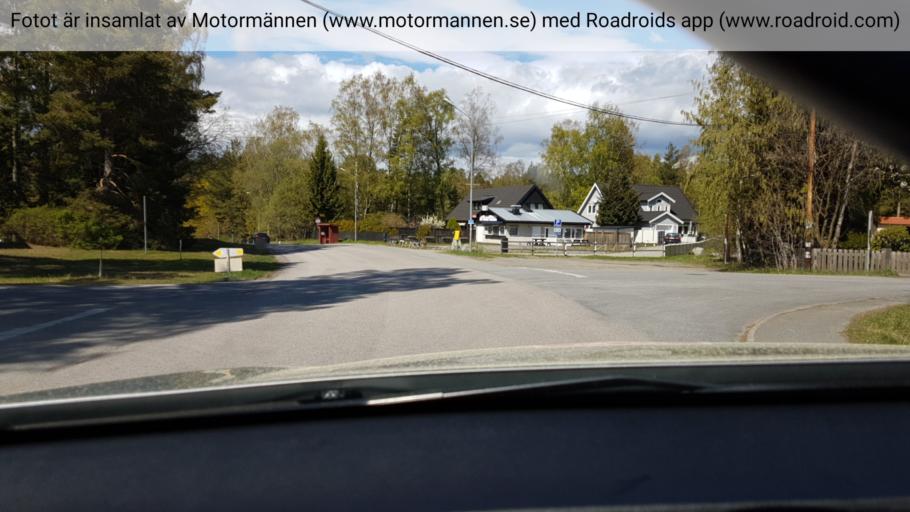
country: SE
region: Stockholm
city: Dalaro
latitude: 59.1435
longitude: 18.4162
